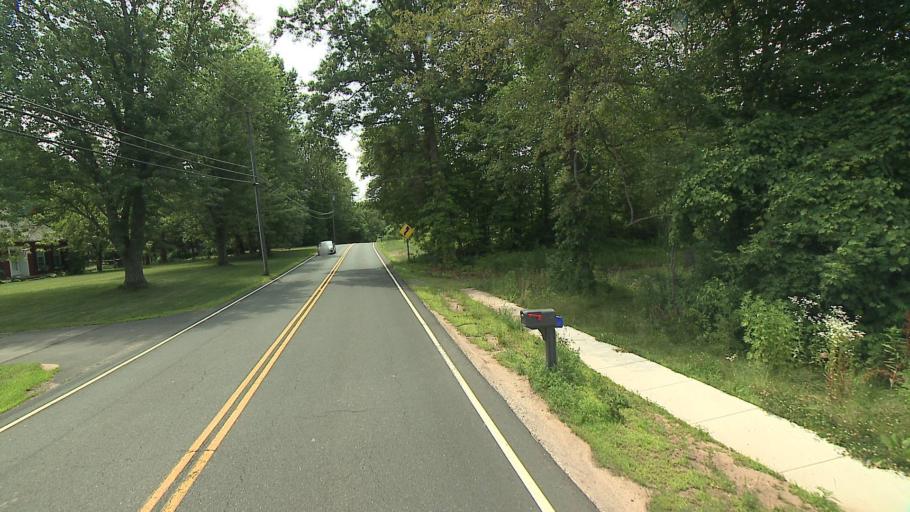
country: US
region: Connecticut
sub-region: Hartford County
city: Suffield Depot
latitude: 41.9805
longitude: -72.6847
